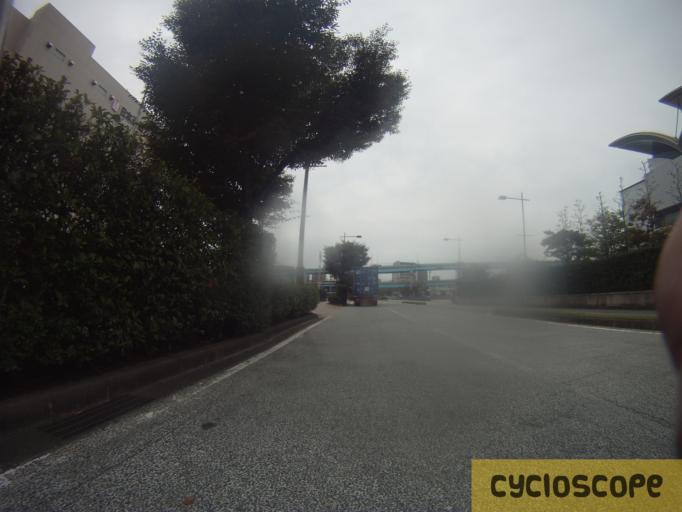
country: JP
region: Fukuoka
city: Fukuoka-shi
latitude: 33.6061
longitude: 130.4057
